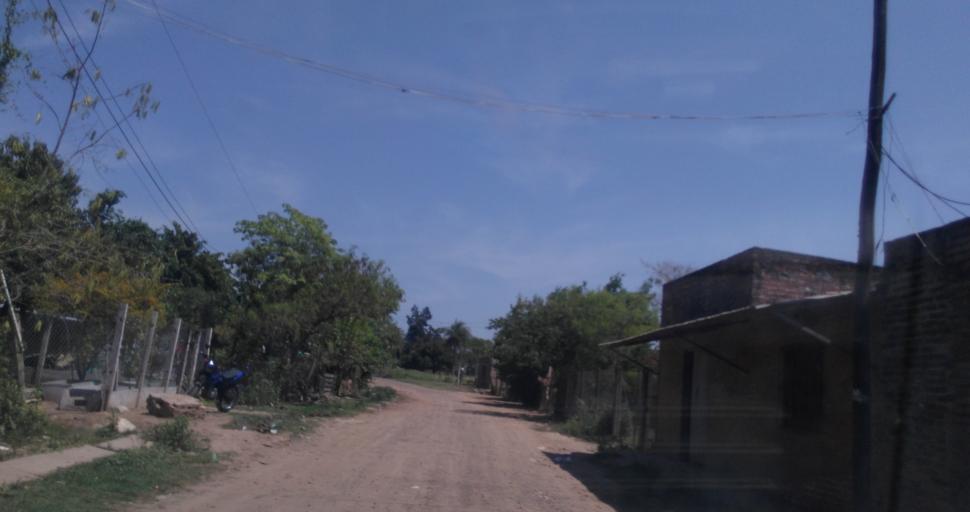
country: AR
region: Chaco
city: Fontana
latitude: -27.4220
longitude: -59.0132
